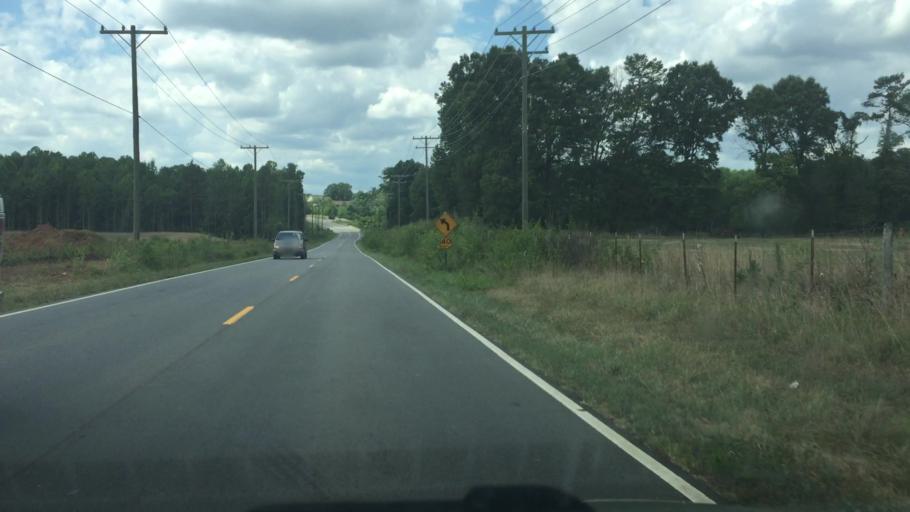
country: US
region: North Carolina
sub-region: Mecklenburg County
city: Huntersville
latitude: 35.4165
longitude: -80.7487
